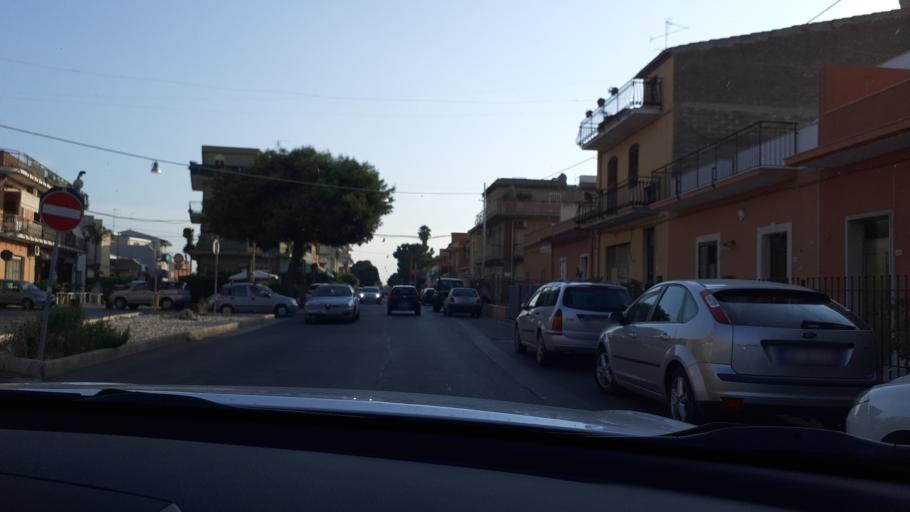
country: IT
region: Sicily
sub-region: Provincia di Siracusa
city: Cassibile
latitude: 36.9758
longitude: 15.1965
